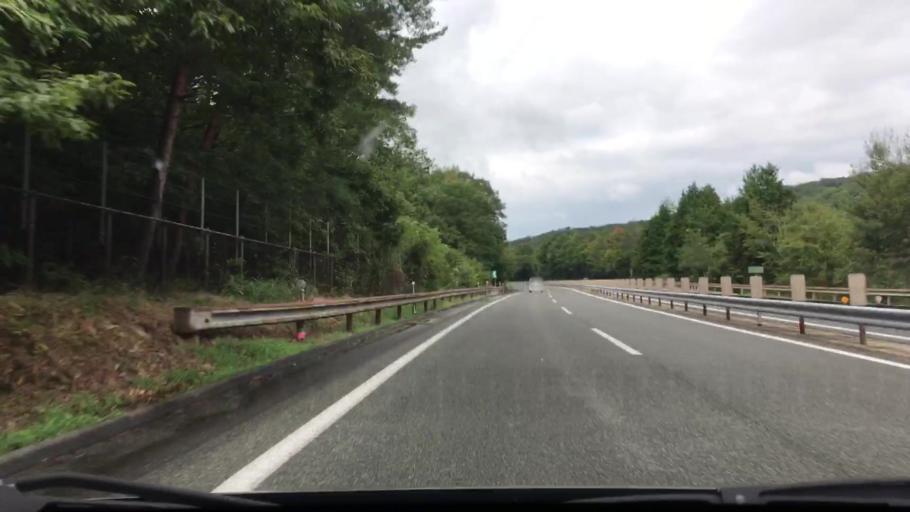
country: JP
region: Hiroshima
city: Miyoshi
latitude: 34.7567
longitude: 132.7484
